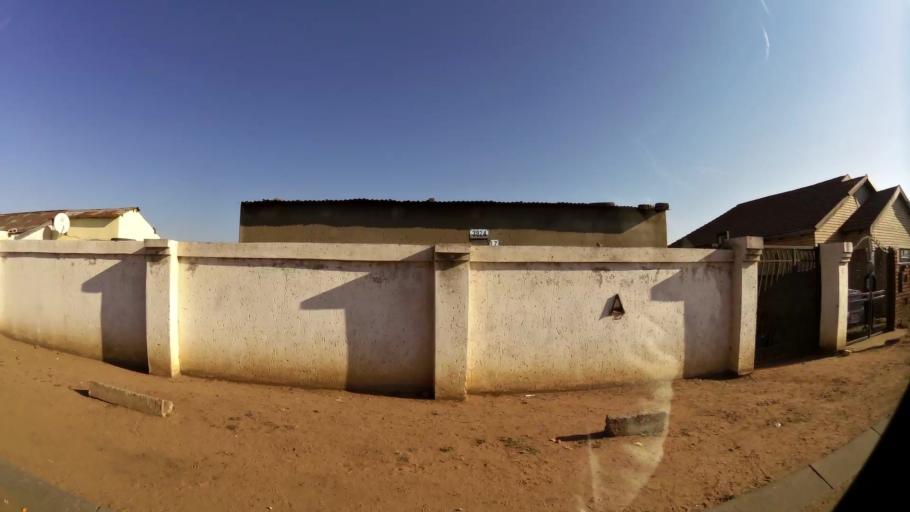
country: ZA
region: Gauteng
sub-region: City of Johannesburg Metropolitan Municipality
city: Soweto
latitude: -26.2357
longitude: 27.9361
